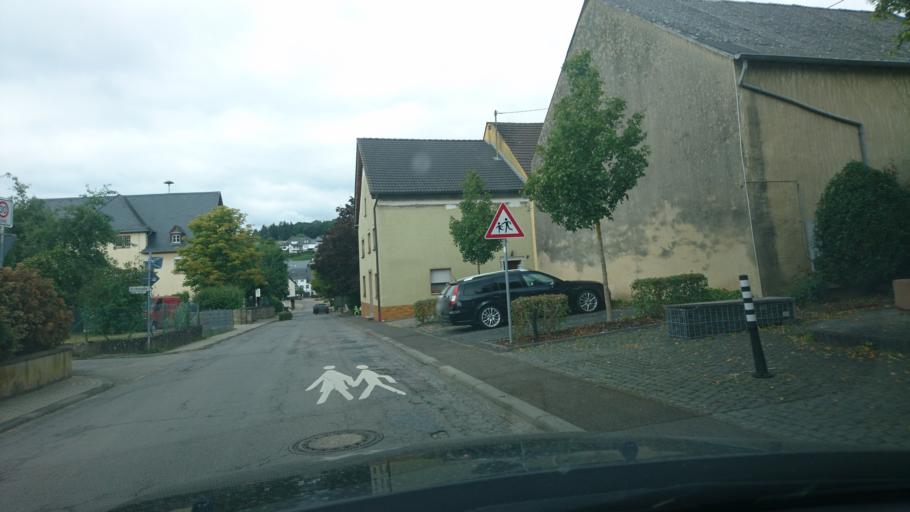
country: DE
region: Rheinland-Pfalz
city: Wiltingen
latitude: 49.6626
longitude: 6.6293
